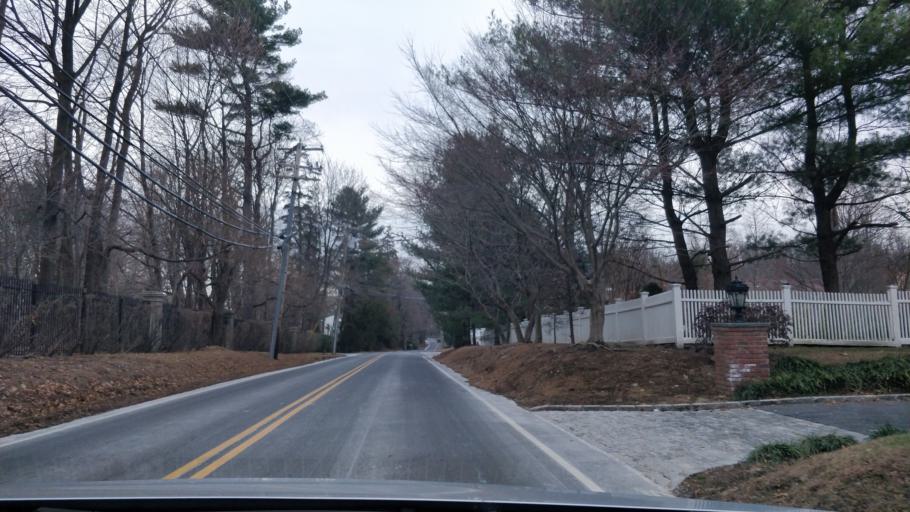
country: US
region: New York
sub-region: Nassau County
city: Glen Cove
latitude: 40.8754
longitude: -73.6411
